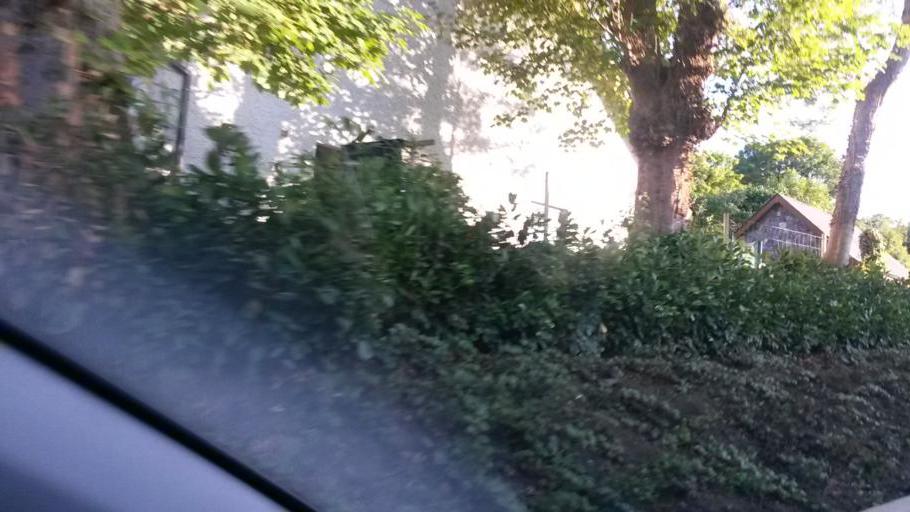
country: IE
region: Leinster
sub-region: An Mhi
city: Ashbourne
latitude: 53.5673
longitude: -6.3796
